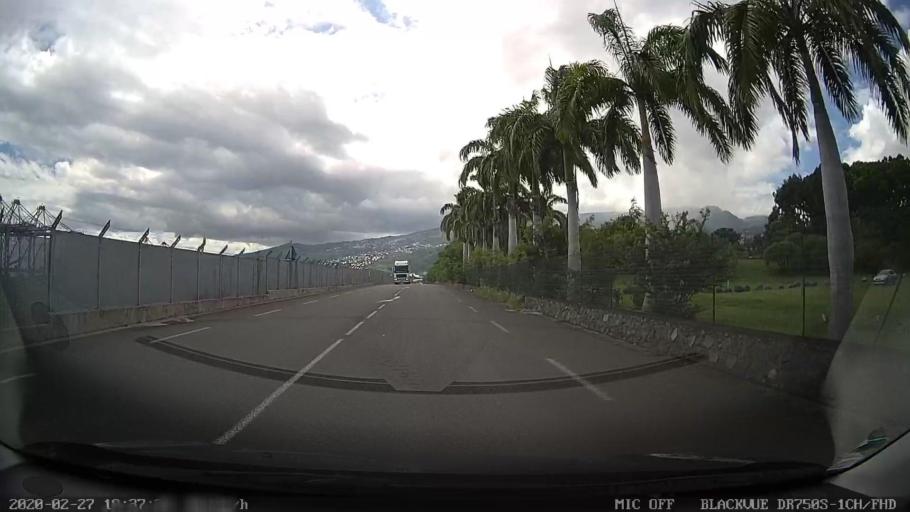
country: RE
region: Reunion
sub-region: Reunion
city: Le Port
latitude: -20.9349
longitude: 55.3119
